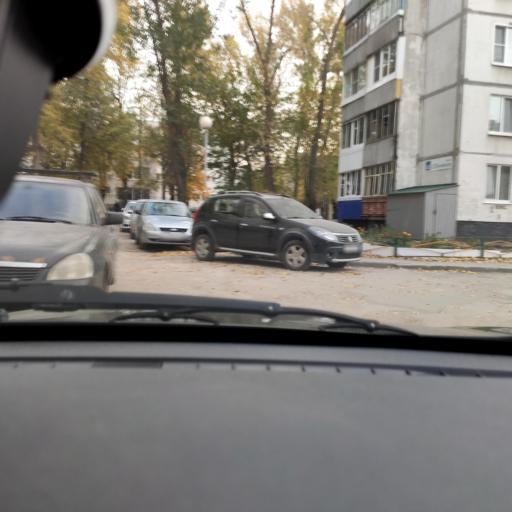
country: RU
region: Samara
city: Tol'yatti
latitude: 53.5097
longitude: 49.2804
